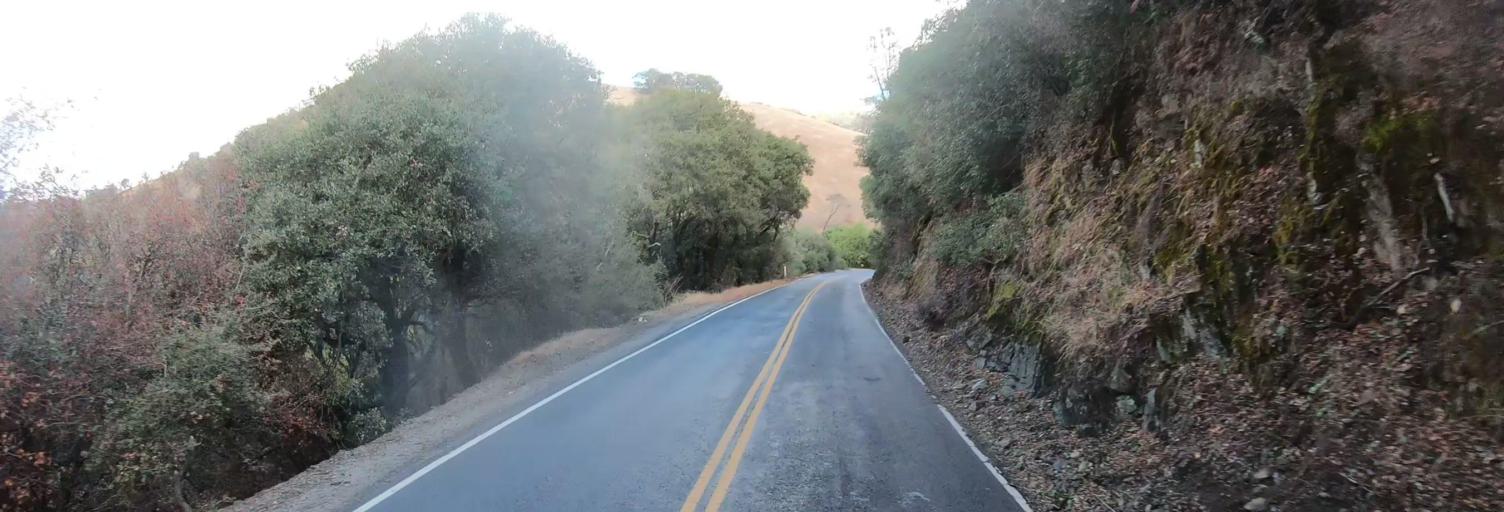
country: US
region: California
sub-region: Santa Clara County
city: East Foothills
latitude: 37.3293
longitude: -121.6784
